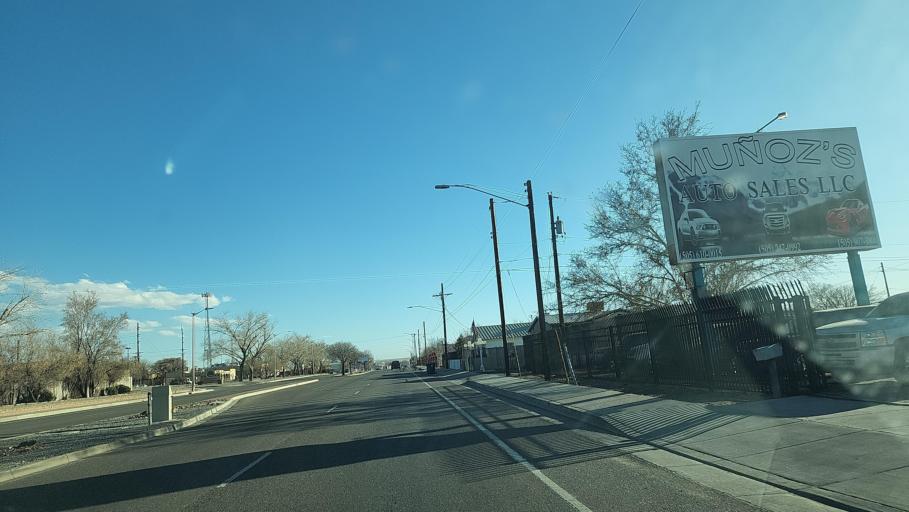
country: US
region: New Mexico
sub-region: Bernalillo County
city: Albuquerque
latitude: 35.0602
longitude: -106.6454
